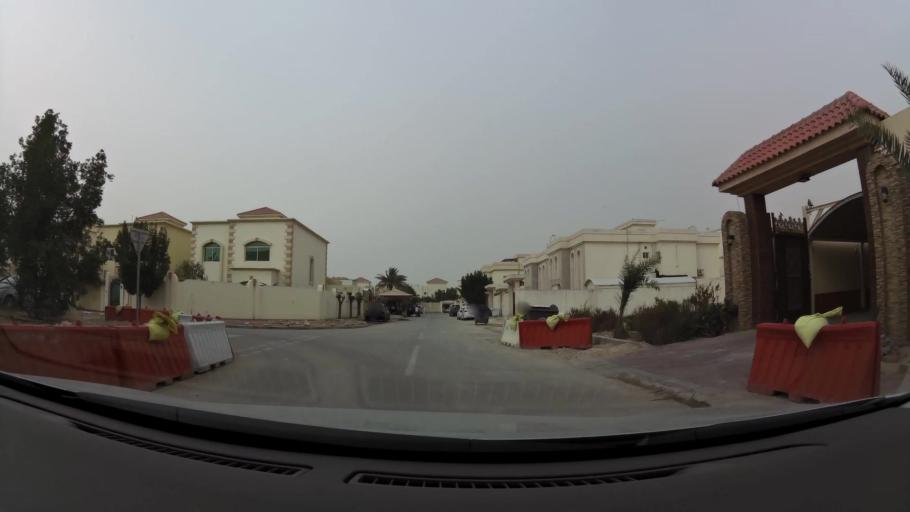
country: QA
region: Baladiyat ad Dawhah
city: Doha
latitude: 25.2429
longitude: 51.5022
